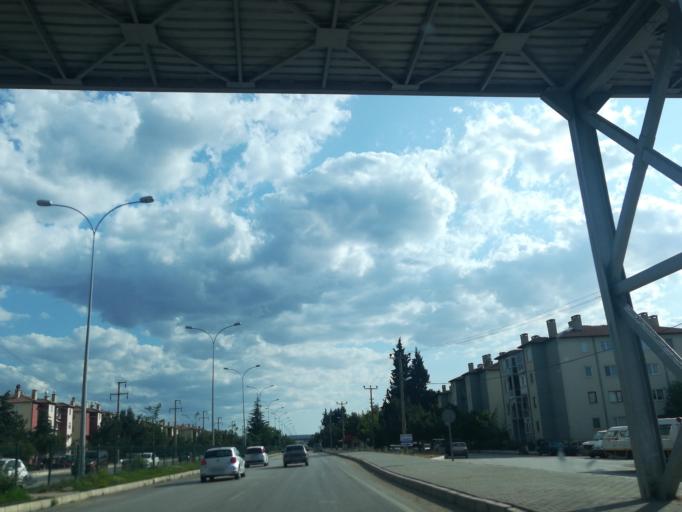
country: TR
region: Afyonkarahisar
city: Dinar
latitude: 38.0642
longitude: 30.1647
